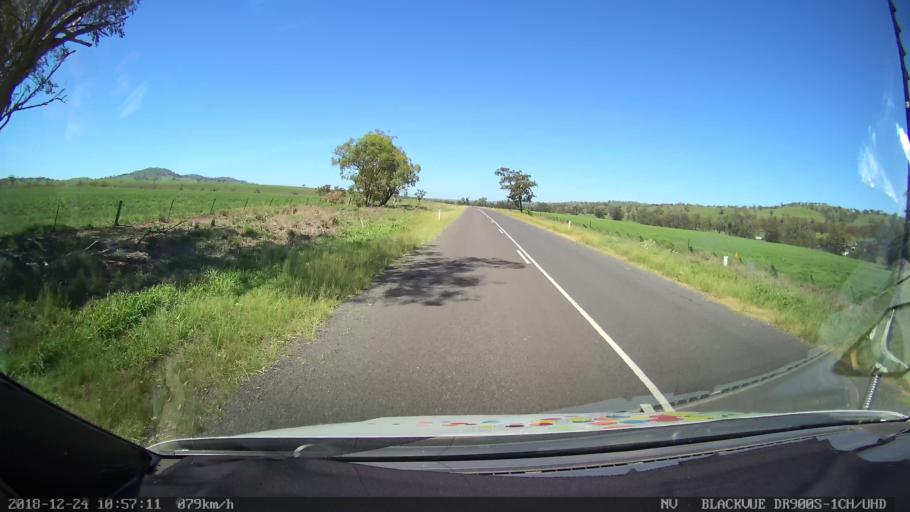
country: AU
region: New South Wales
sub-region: Upper Hunter Shire
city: Merriwa
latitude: -32.0334
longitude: 150.4151
